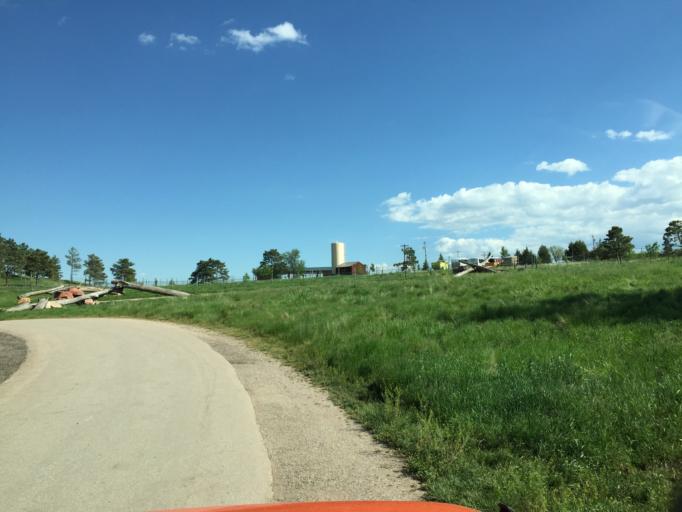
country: US
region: South Dakota
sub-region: Pennington County
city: Colonial Pine Hills
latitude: 43.9778
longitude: -103.2984
